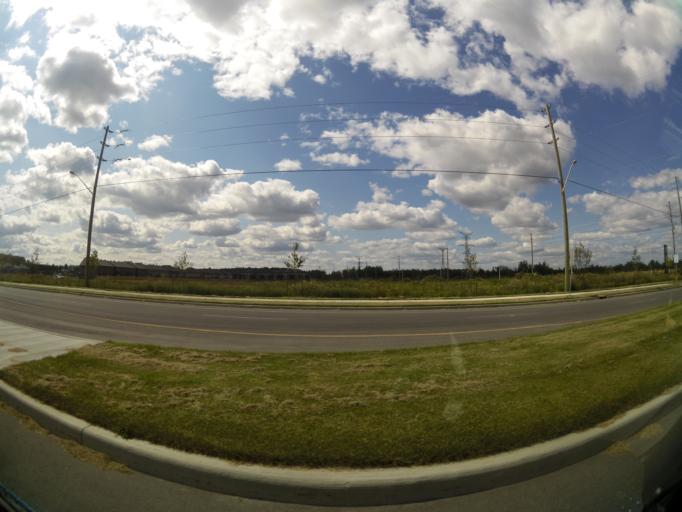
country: CA
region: Ontario
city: Ottawa
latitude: 45.4402
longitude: -75.5087
